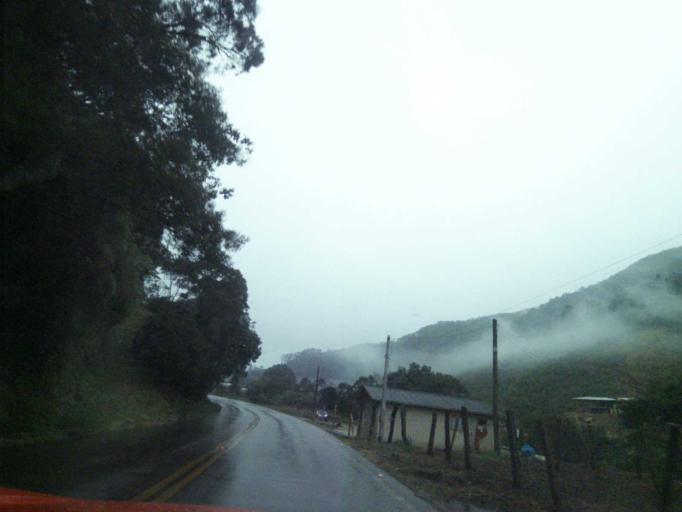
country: BR
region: Santa Catarina
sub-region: Anitapolis
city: Anitapolis
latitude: -27.8322
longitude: -49.0518
